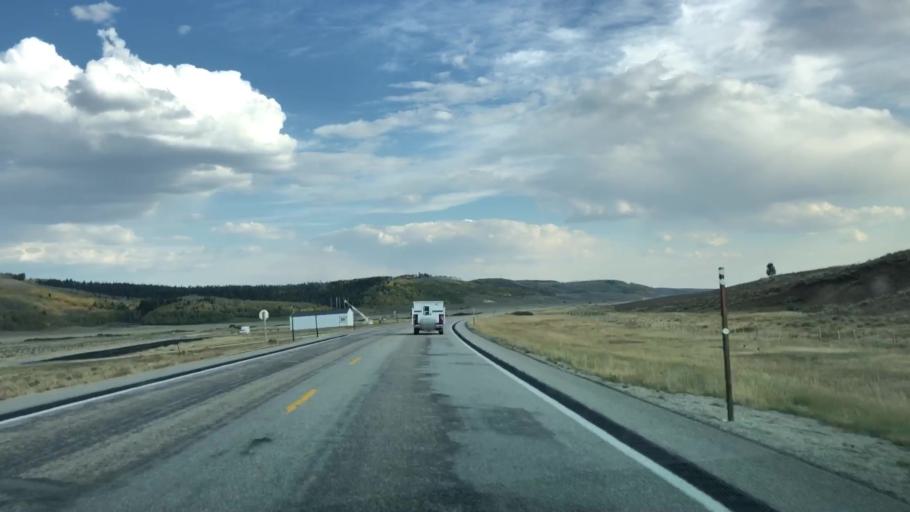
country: US
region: Wyoming
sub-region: Sublette County
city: Pinedale
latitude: 43.1173
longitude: -110.1779
